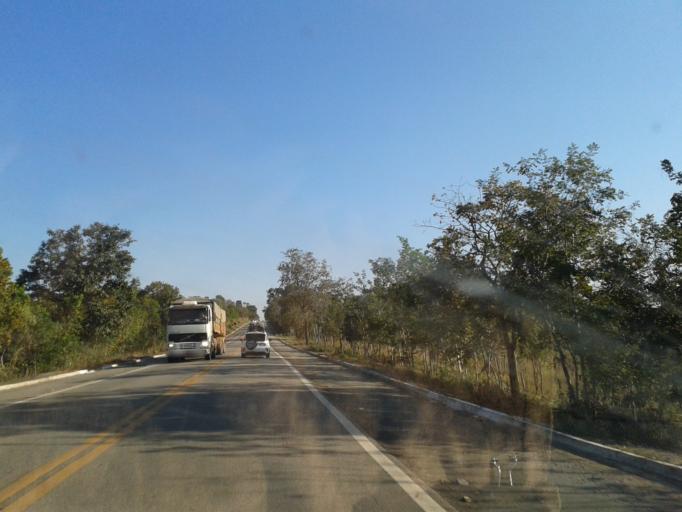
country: BR
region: Goias
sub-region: Mozarlandia
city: Mozarlandia
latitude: -15.2876
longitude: -50.4704
